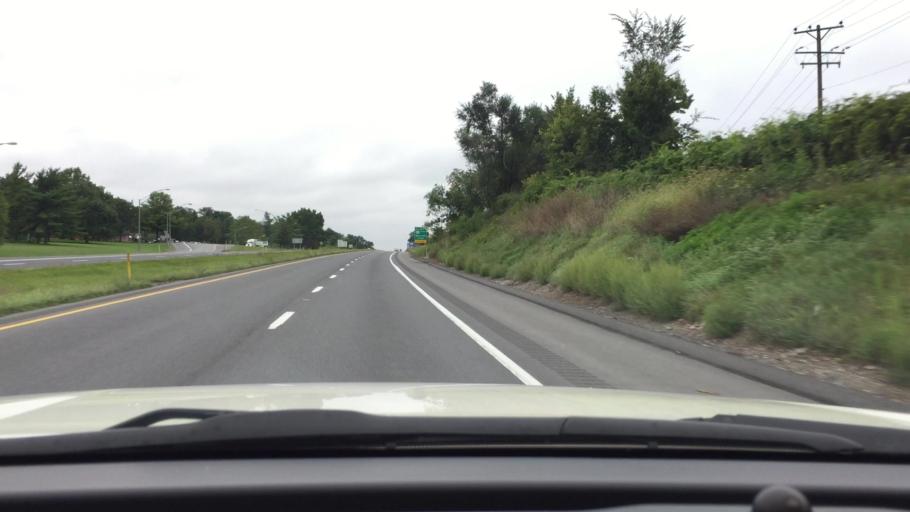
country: US
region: Maryland
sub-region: Washington County
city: Hancock
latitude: 39.7402
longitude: -78.1815
